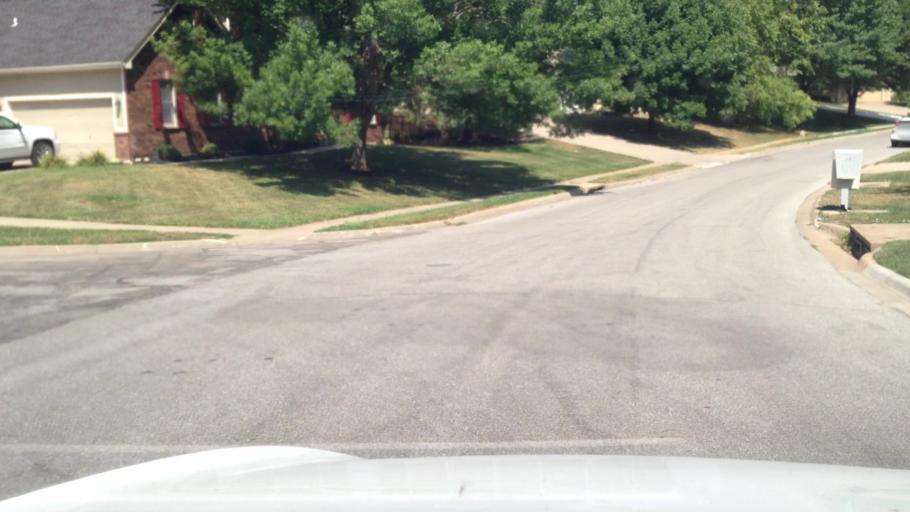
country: US
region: Kansas
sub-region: Douglas County
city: Lawrence
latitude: 38.9464
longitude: -95.3003
